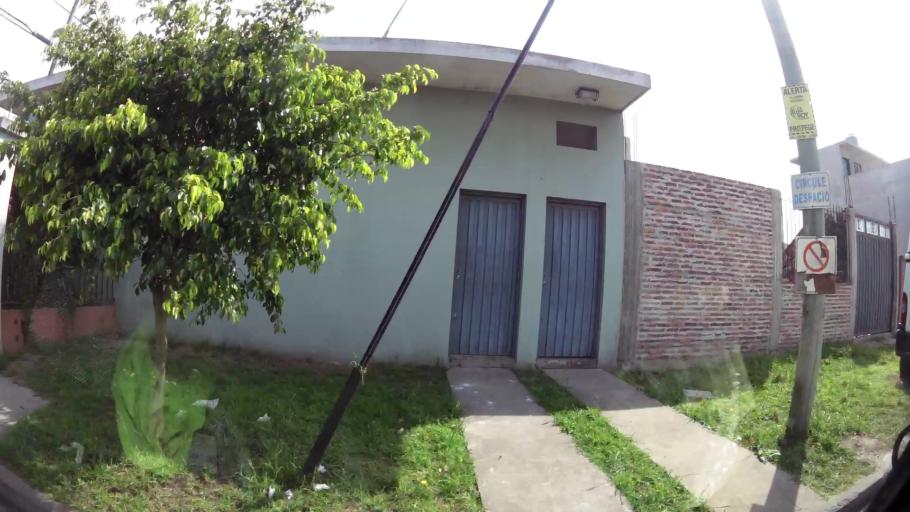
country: AR
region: Buenos Aires
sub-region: Partido de Quilmes
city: Quilmes
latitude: -34.7632
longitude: -58.2476
